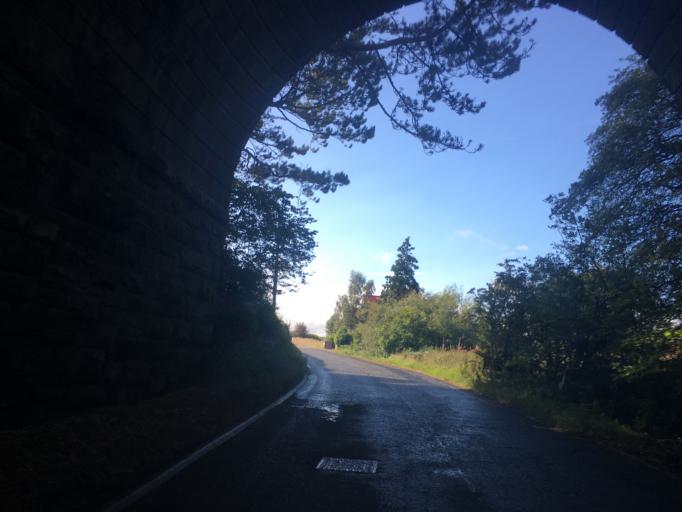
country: GB
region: Scotland
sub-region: Edinburgh
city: Kirkliston
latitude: 55.9662
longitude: -3.3759
